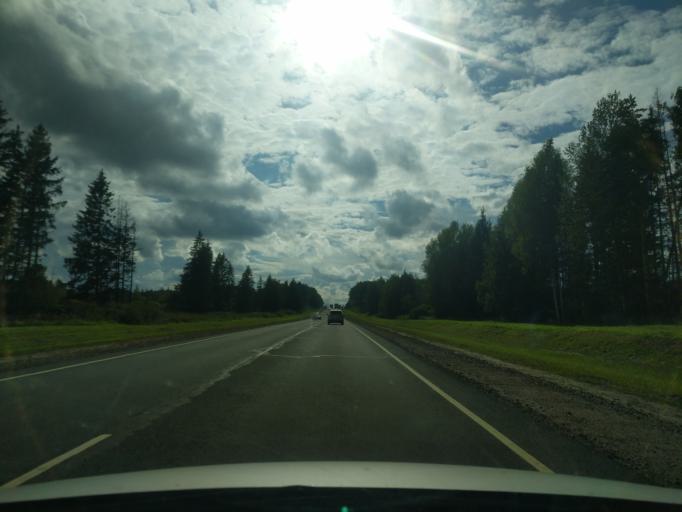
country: RU
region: Jaroslavl
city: Nekrasovskoye
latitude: 57.6222
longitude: 40.3595
